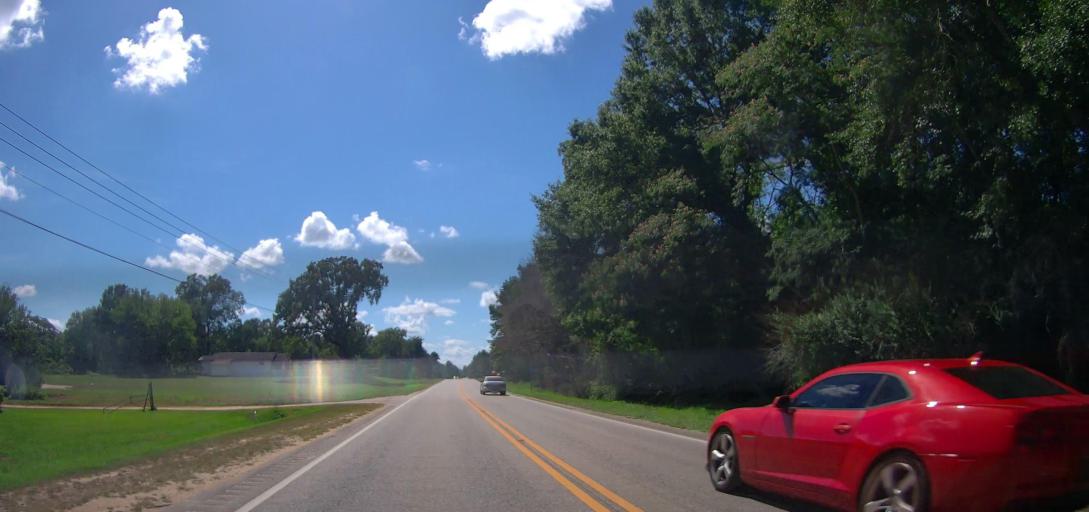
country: US
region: Alabama
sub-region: Macon County
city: Tuskegee
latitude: 32.3752
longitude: -85.8470
